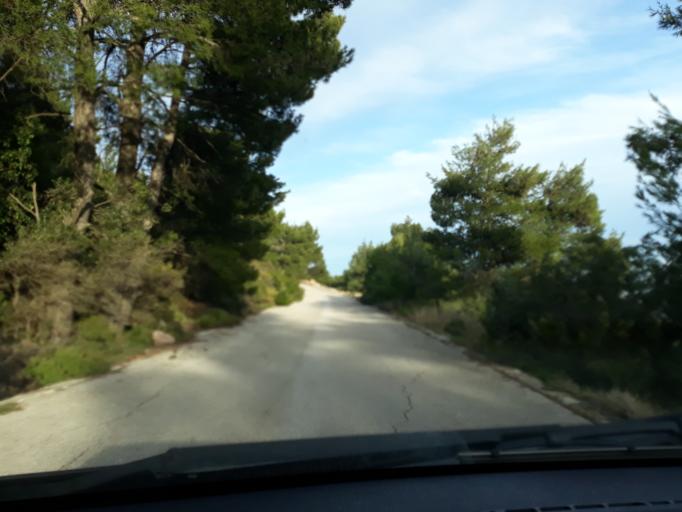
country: GR
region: Attica
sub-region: Nomarchia Anatolikis Attikis
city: Afidnes
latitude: 38.2144
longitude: 23.8120
